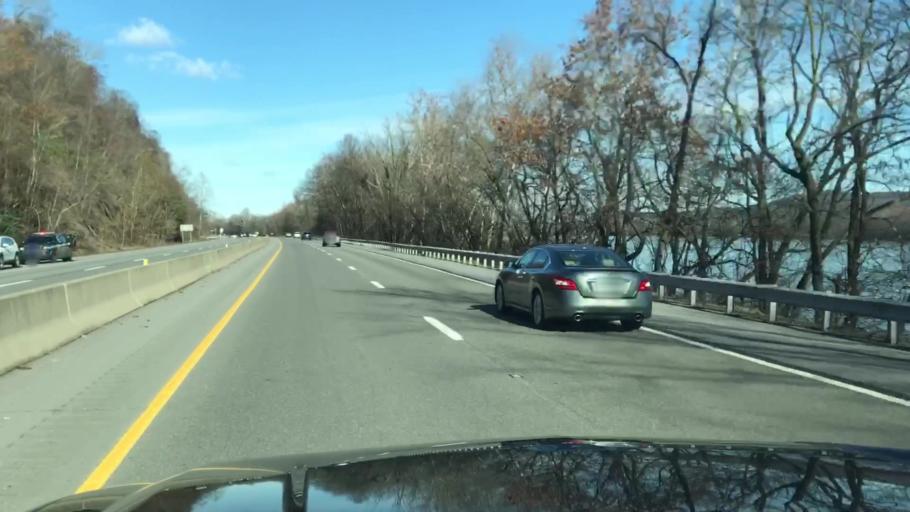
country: US
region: Pennsylvania
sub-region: Snyder County
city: Selinsgrove
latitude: 40.7433
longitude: -76.8571
